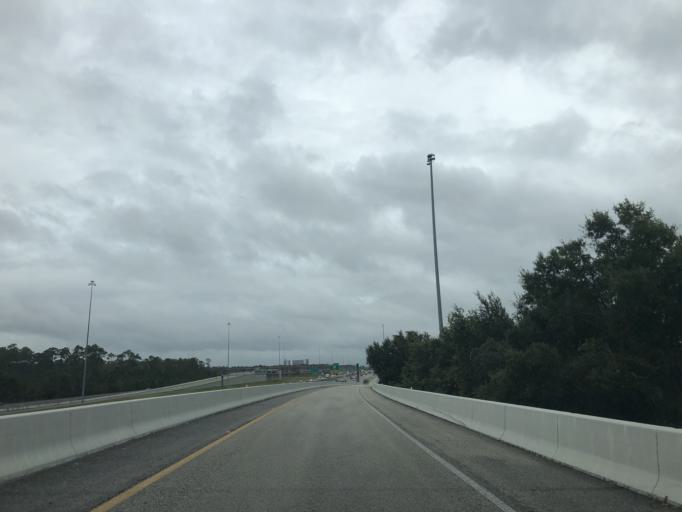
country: US
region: Florida
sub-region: Osceola County
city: Celebration
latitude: 28.3378
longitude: -81.5399
